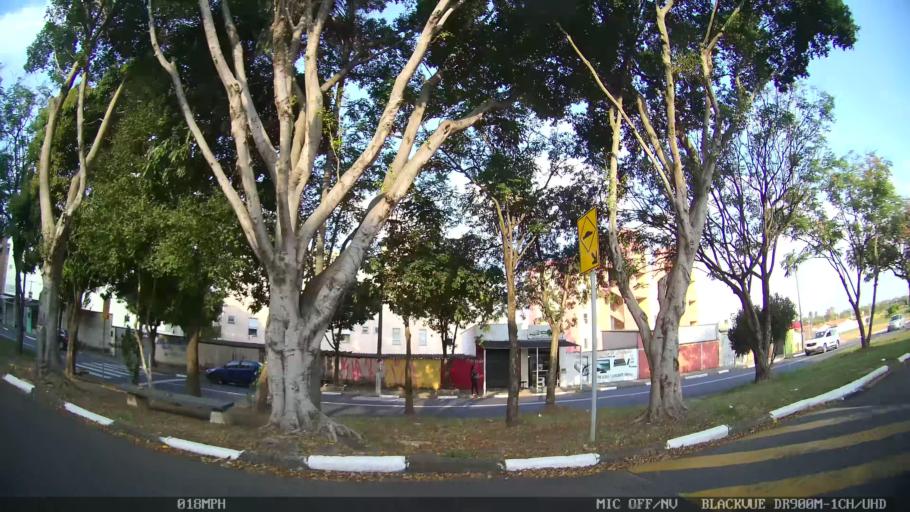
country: BR
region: Sao Paulo
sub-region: Hortolandia
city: Hortolandia
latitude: -22.8678
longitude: -47.1557
